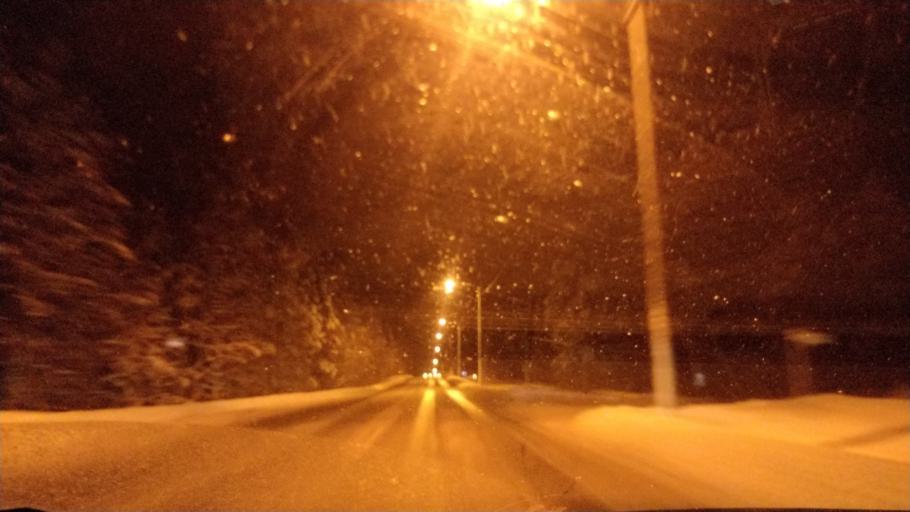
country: FI
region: Lapland
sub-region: Rovaniemi
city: Rovaniemi
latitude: 66.3217
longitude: 25.3576
